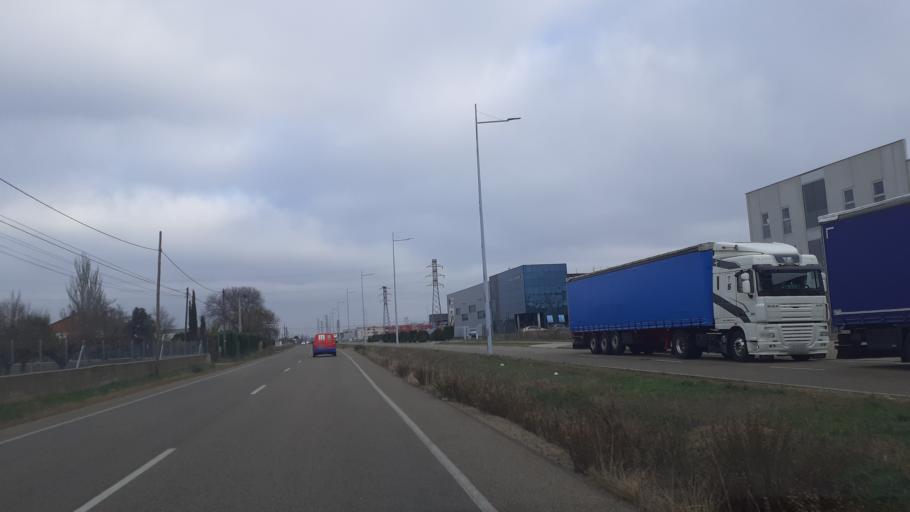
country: ES
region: Castille and Leon
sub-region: Provincia de Leon
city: Onzonilla
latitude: 42.5450
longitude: -5.5877
